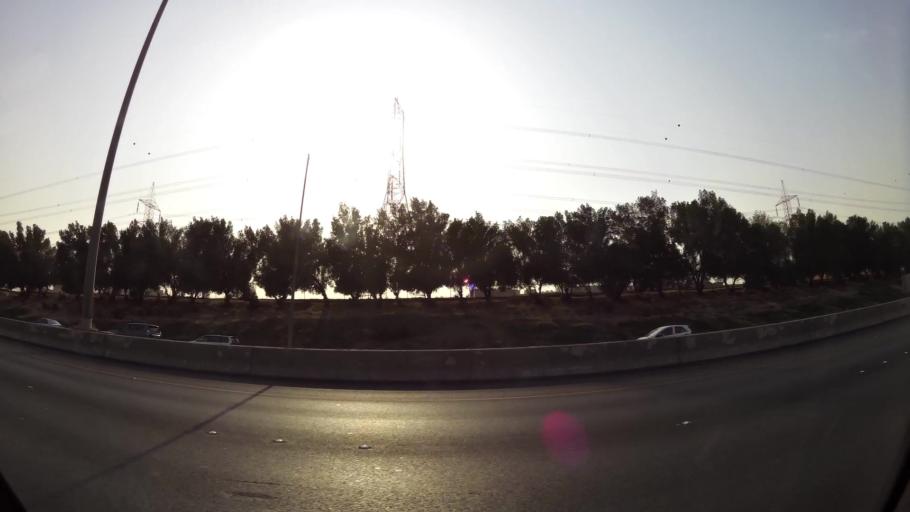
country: KW
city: Bayan
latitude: 29.3014
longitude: 48.0247
